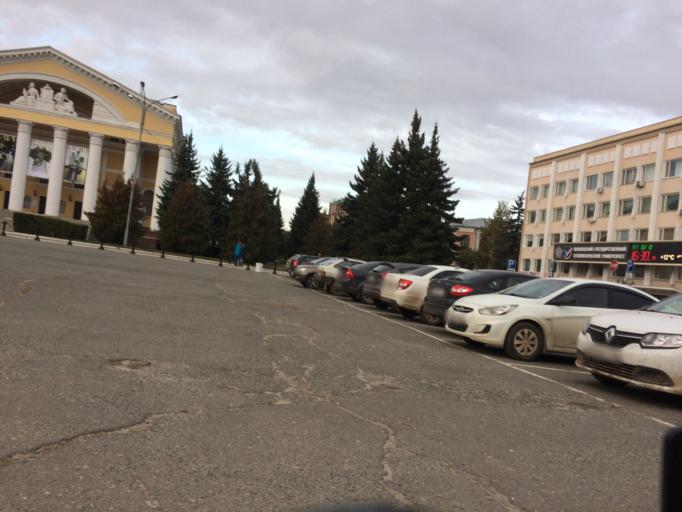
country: RU
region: Mariy-El
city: Yoshkar-Ola
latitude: 56.6305
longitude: 47.8911
